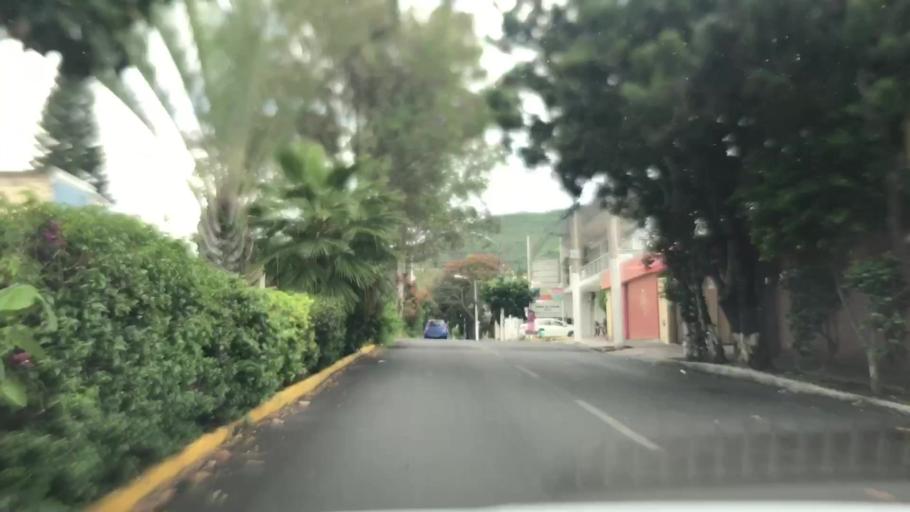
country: MX
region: Jalisco
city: Guadalajara
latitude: 20.6243
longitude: -103.4095
